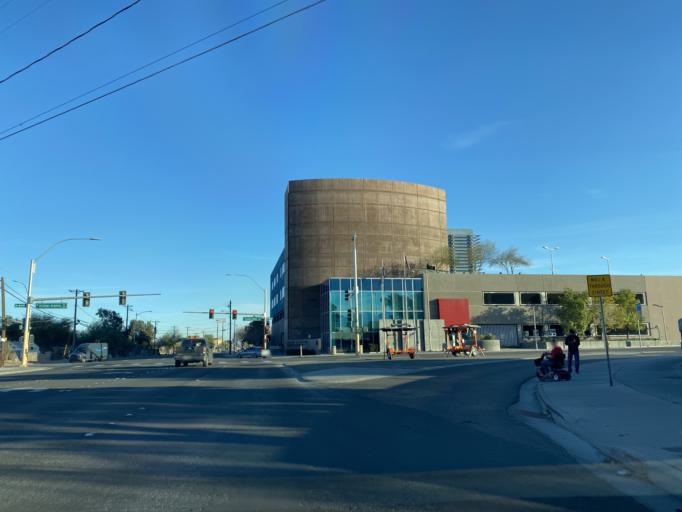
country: US
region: Nevada
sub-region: Clark County
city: Las Vegas
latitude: 36.1763
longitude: -115.1409
